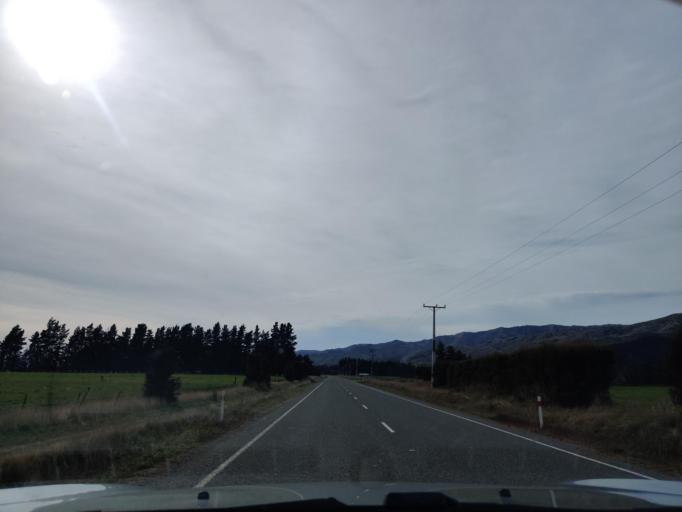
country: NZ
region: Tasman
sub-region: Tasman District
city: Brightwater
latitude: -41.6532
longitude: 173.2662
